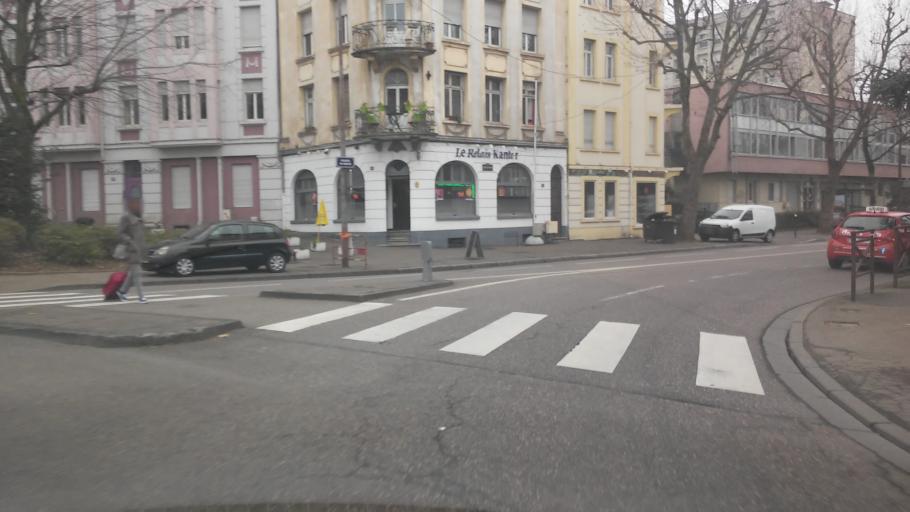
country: FR
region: Lorraine
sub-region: Departement de la Moselle
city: Metz
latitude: 49.1058
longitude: 6.1742
